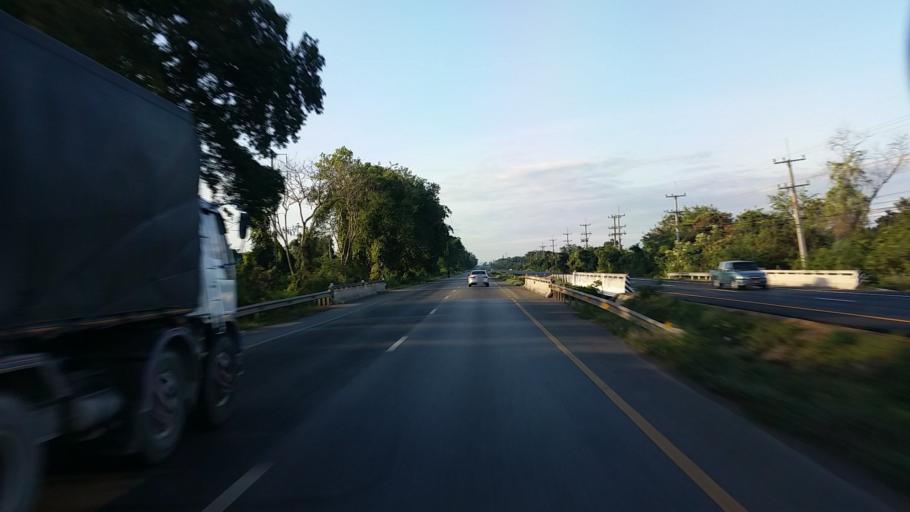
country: TH
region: Lop Buri
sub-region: Amphoe Tha Luang
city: Tha Luang
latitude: 15.1061
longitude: 101.0233
